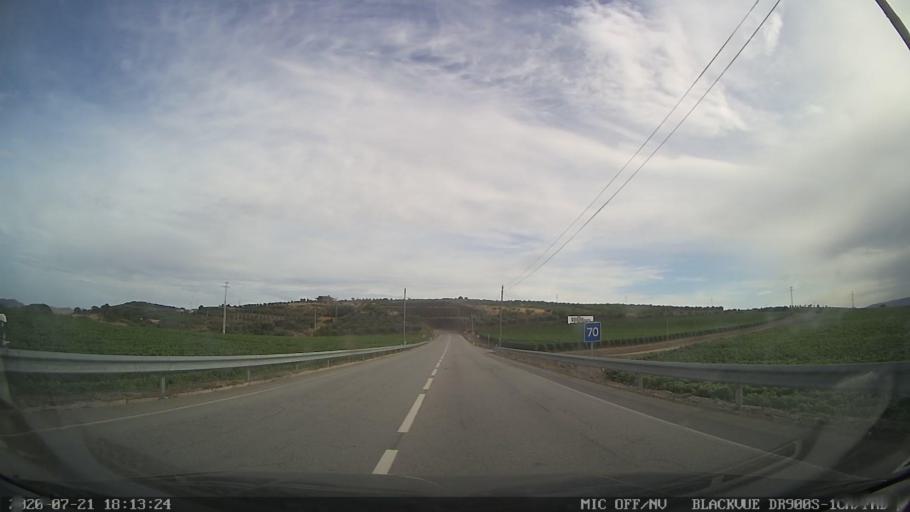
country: PT
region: Viseu
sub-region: Sao Joao da Pesqueira
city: Sao Joao da Pesqueira
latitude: 41.1309
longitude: -7.3982
